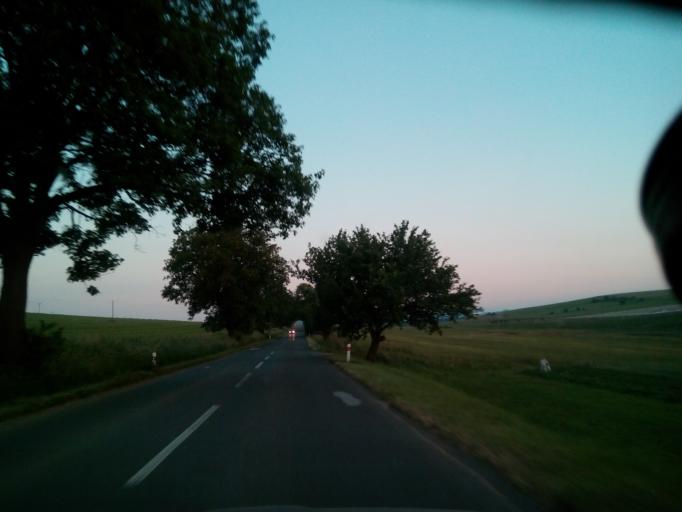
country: SK
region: Presovsky
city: Lubica
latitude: 49.0418
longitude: 20.4380
